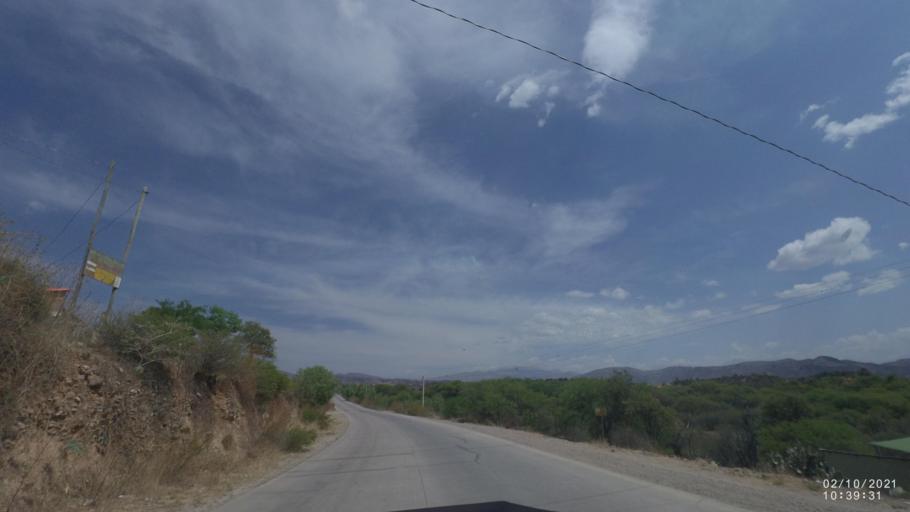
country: BO
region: Cochabamba
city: Capinota
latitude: -17.6287
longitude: -66.2748
